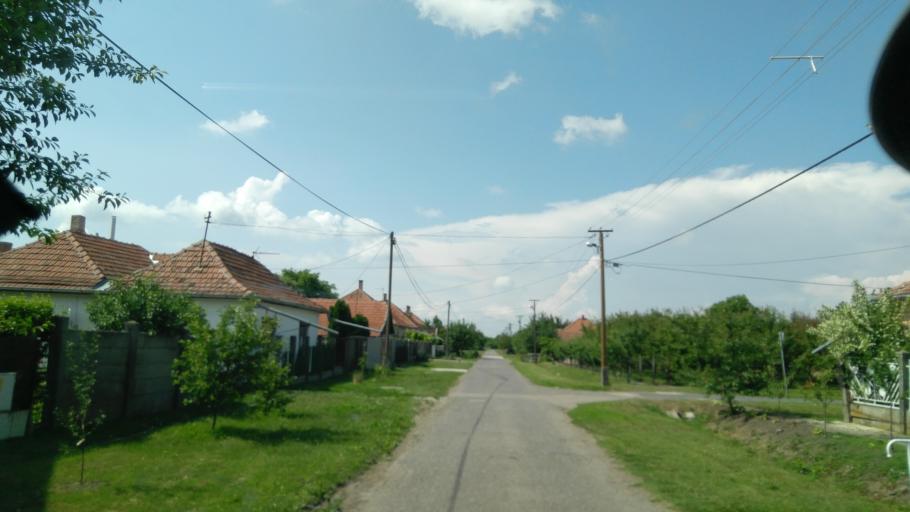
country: HU
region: Bekes
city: Doboz
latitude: 46.7375
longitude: 21.2291
